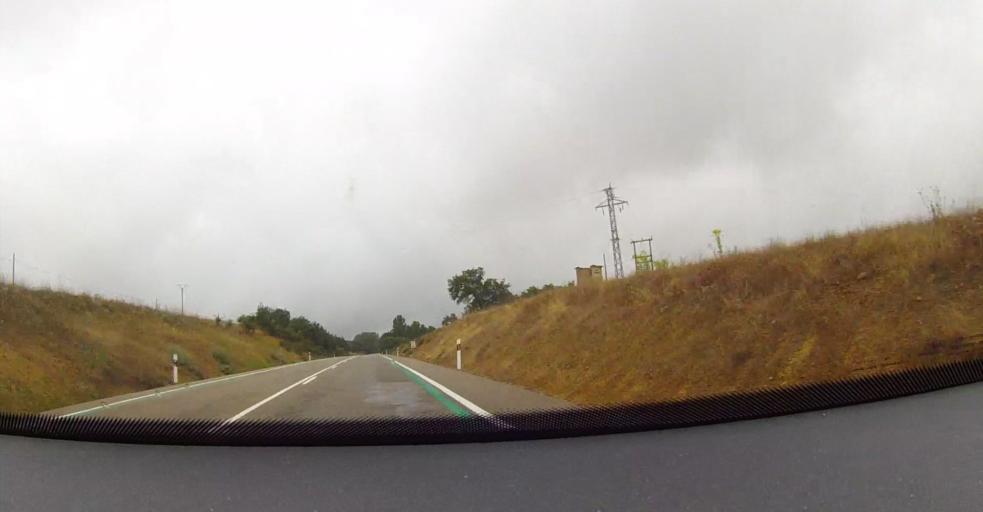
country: ES
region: Castille and Leon
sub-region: Provincia de Palencia
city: Saldana
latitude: 42.5563
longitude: -4.7411
